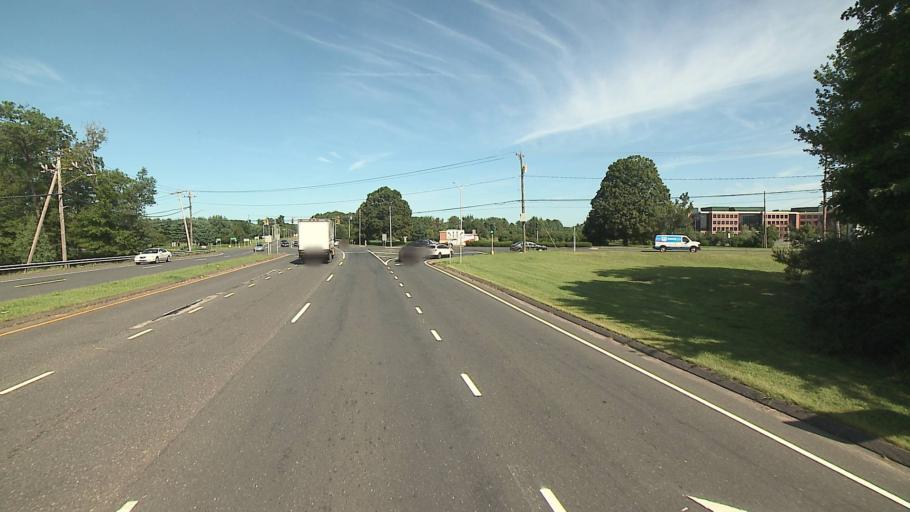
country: US
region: Connecticut
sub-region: Hartford County
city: Tariffville
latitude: 41.8754
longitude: -72.7294
